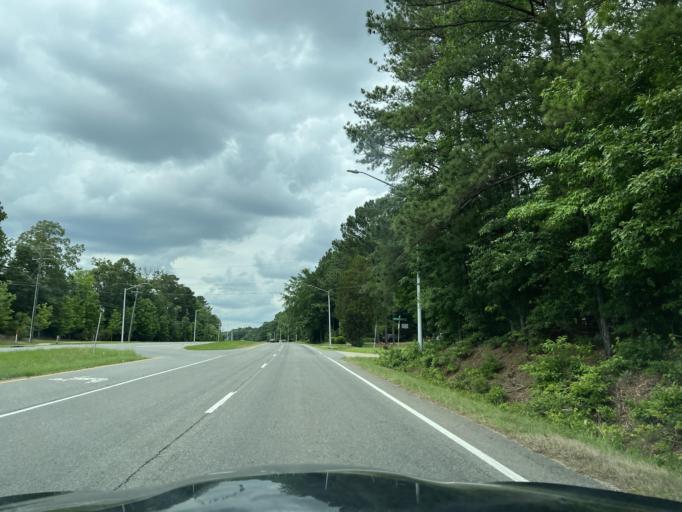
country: US
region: North Carolina
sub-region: Durham County
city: Durham
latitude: 35.9383
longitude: -78.8873
